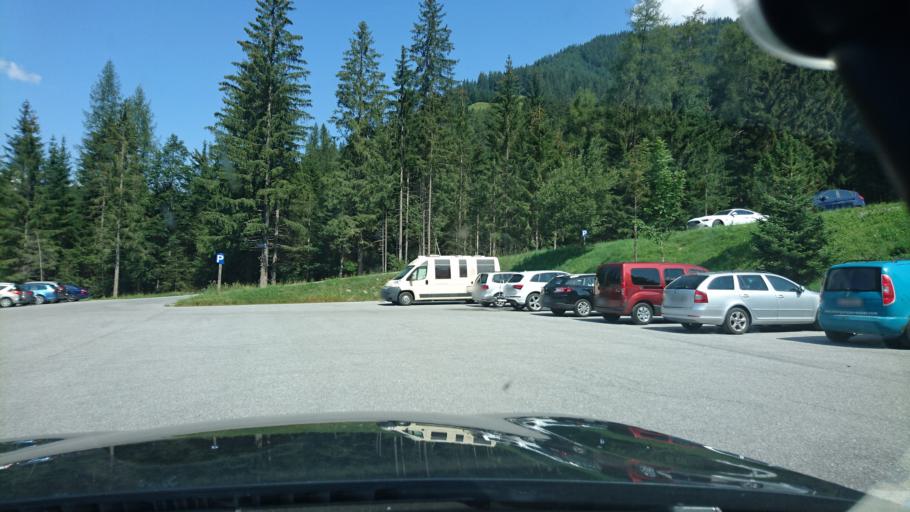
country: AT
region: Tyrol
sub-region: Politischer Bezirk Reutte
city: Ehrwald
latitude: 47.3885
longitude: 10.9386
